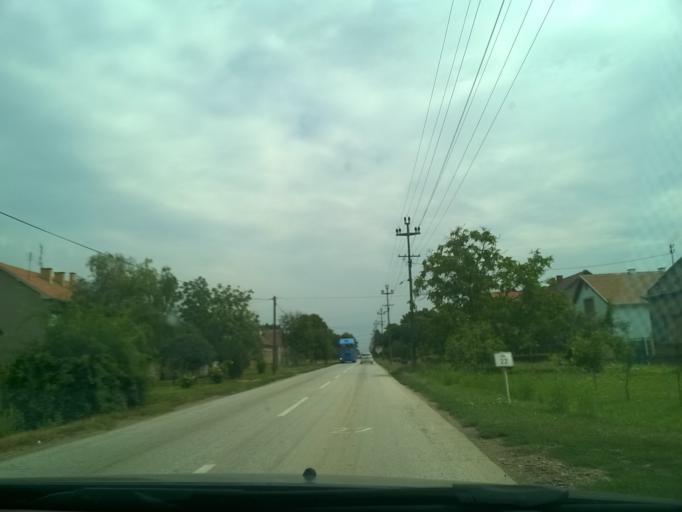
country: RS
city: Sutjeska
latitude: 45.3803
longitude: 20.6951
